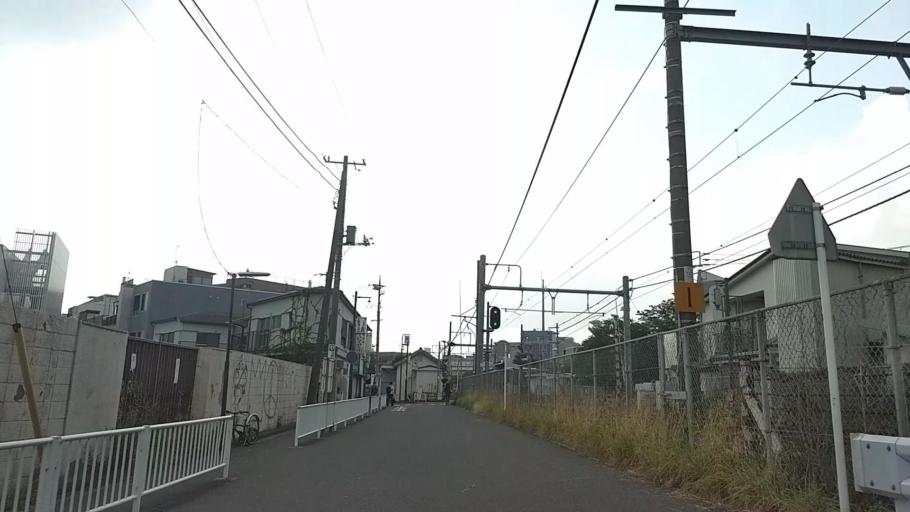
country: JP
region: Kanagawa
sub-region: Kawasaki-shi
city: Kawasaki
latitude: 35.4979
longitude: 139.6804
